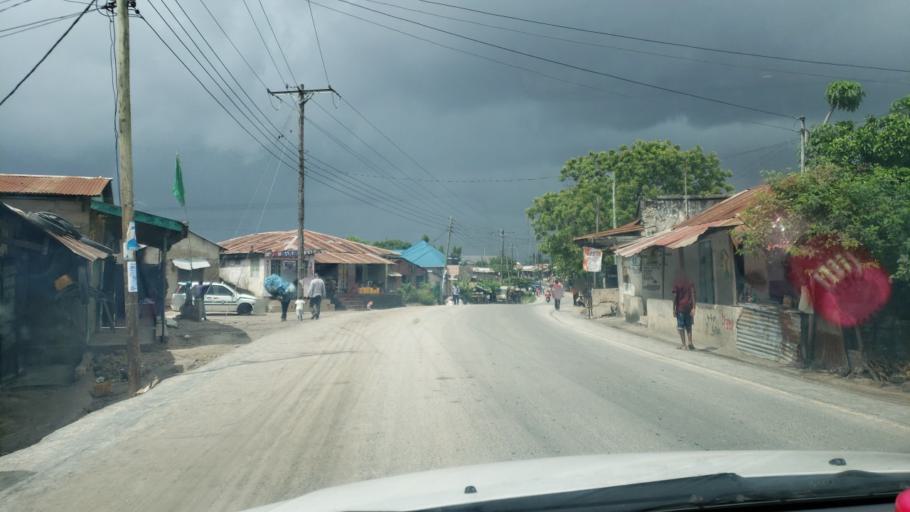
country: TZ
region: Dar es Salaam
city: Magomeni
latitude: -6.8072
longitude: 39.2423
